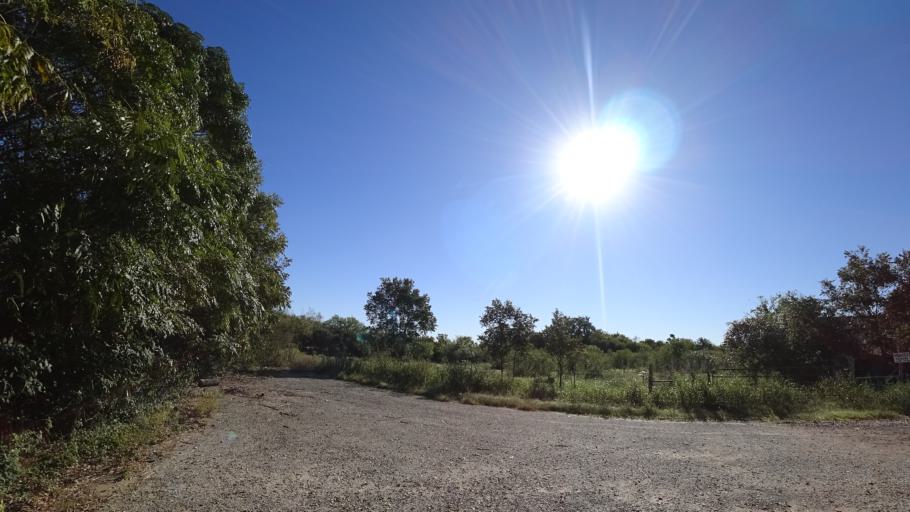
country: US
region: Texas
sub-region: Travis County
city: Hornsby Bend
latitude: 30.2370
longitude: -97.6536
